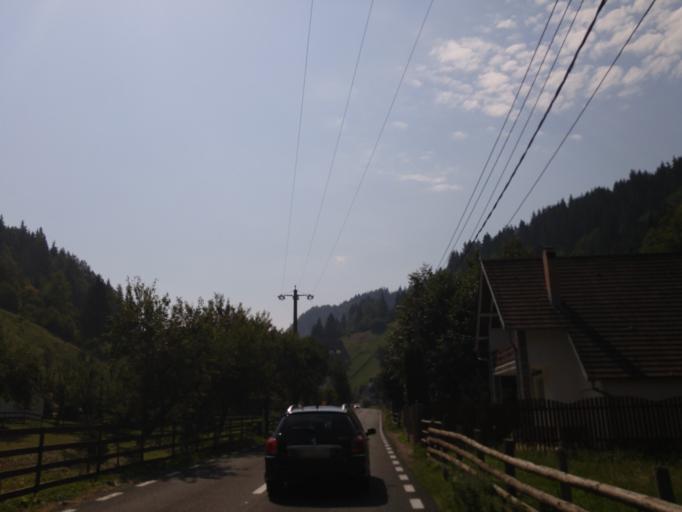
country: RO
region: Brasov
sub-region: Comuna Fundata
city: Fundata
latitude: 45.4614
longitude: 25.3078
